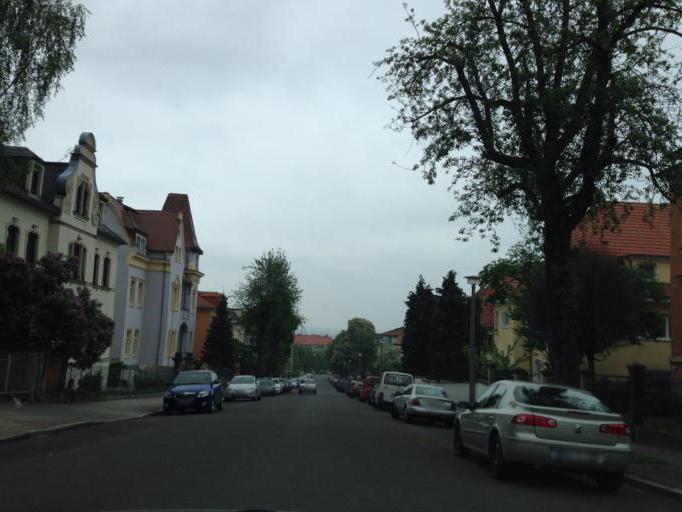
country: DE
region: Saxony
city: Bannewitz
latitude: 51.0249
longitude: 13.7135
